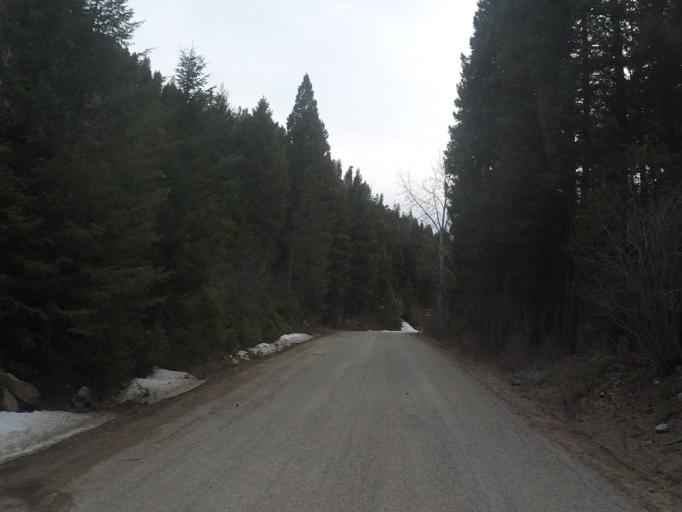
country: US
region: Montana
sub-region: Ravalli County
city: Hamilton
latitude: 45.8450
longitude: -114.0357
